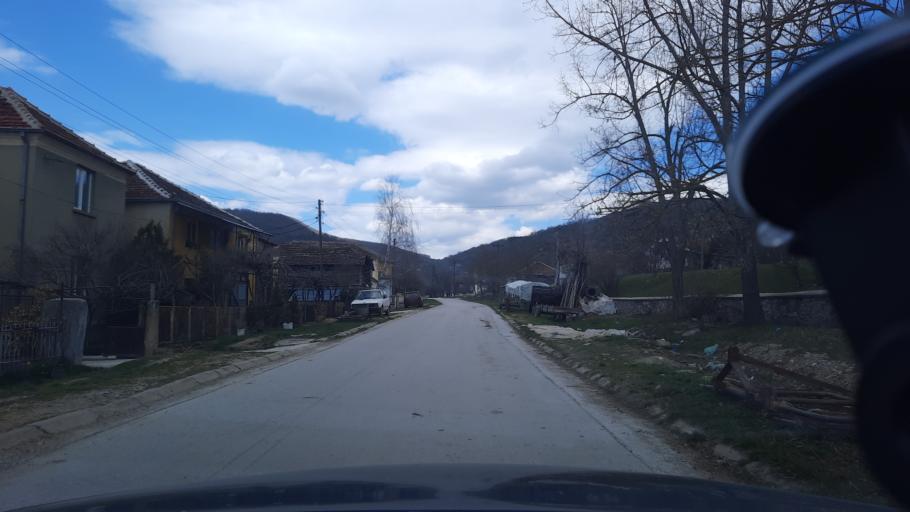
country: MK
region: Demir Hisar
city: Sopotnica
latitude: 41.2939
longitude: 21.1562
